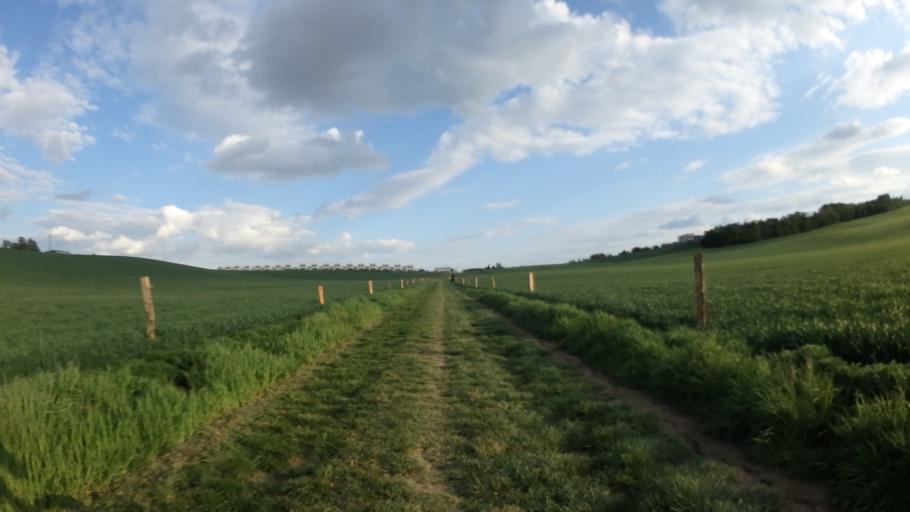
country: CZ
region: South Moravian
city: Moravany
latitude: 49.1568
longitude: 16.5766
